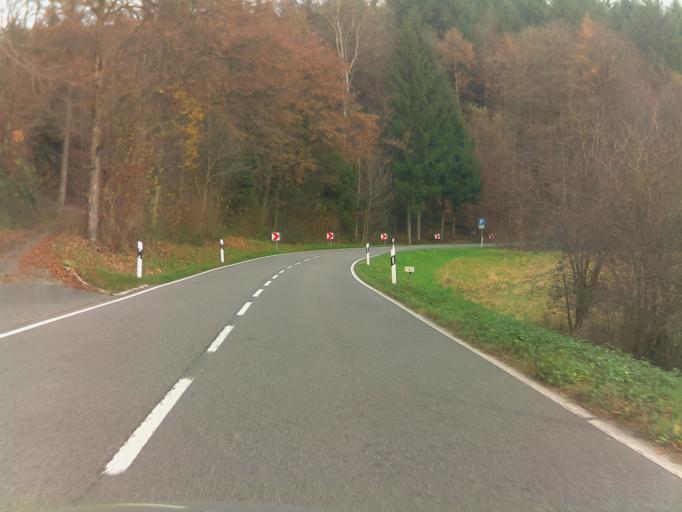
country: DE
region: Baden-Wuerttemberg
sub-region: Karlsruhe Region
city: Spechbach
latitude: 49.3814
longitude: 8.9061
